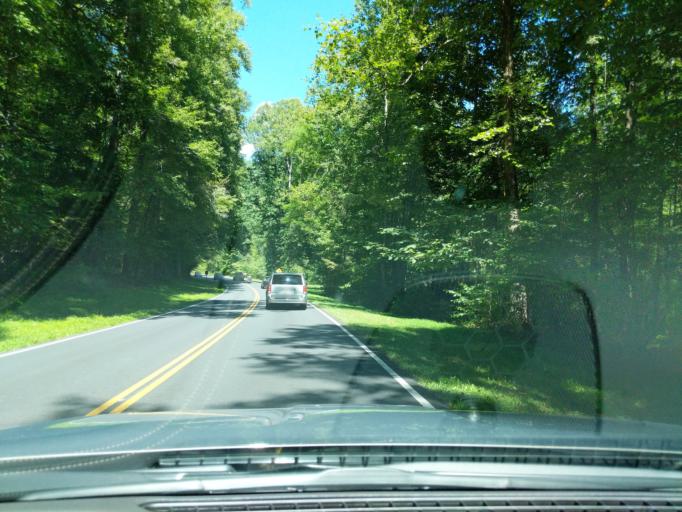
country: US
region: North Carolina
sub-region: Swain County
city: Cherokee
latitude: 35.5386
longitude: -83.3000
